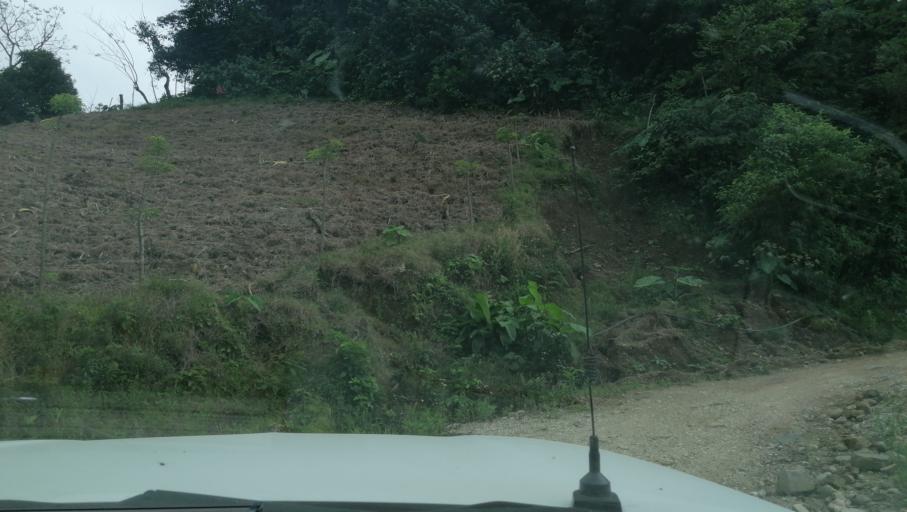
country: MX
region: Chiapas
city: Ostuacan
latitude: 17.3486
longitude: -93.3086
